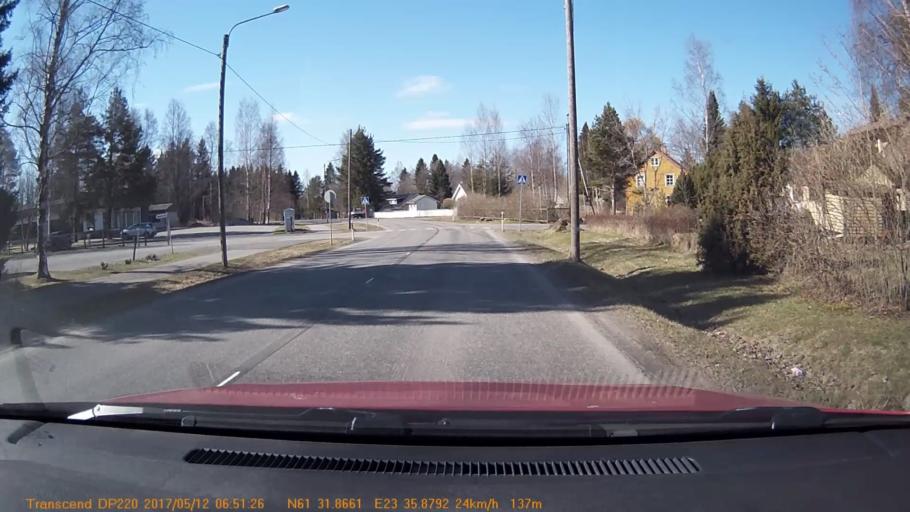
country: FI
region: Pirkanmaa
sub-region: Tampere
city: Yloejaervi
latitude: 61.5311
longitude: 23.5981
